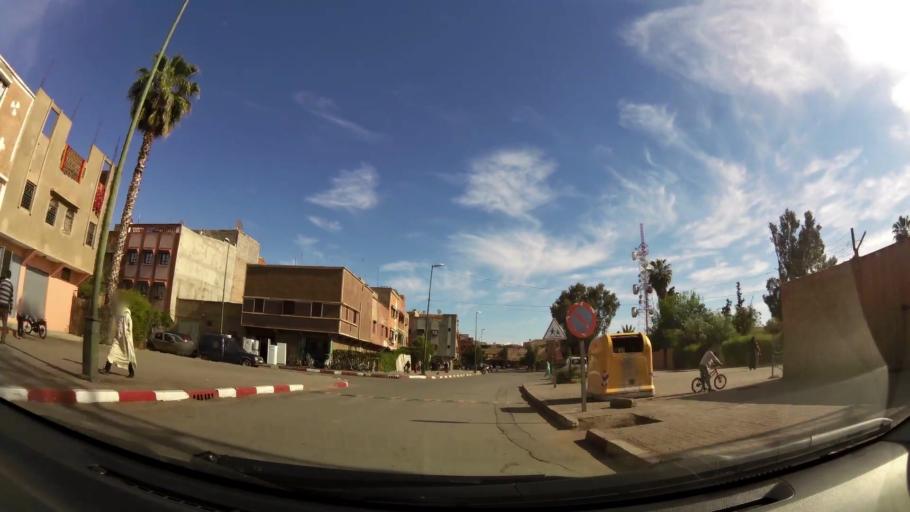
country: MA
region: Marrakech-Tensift-Al Haouz
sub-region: Marrakech
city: Marrakesh
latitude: 31.6085
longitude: -7.9612
